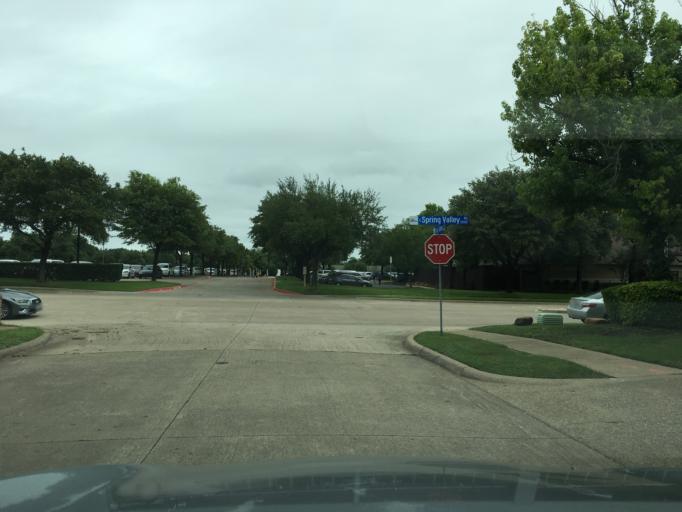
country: US
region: Texas
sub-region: Dallas County
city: Richardson
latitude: 32.9381
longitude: -96.6850
